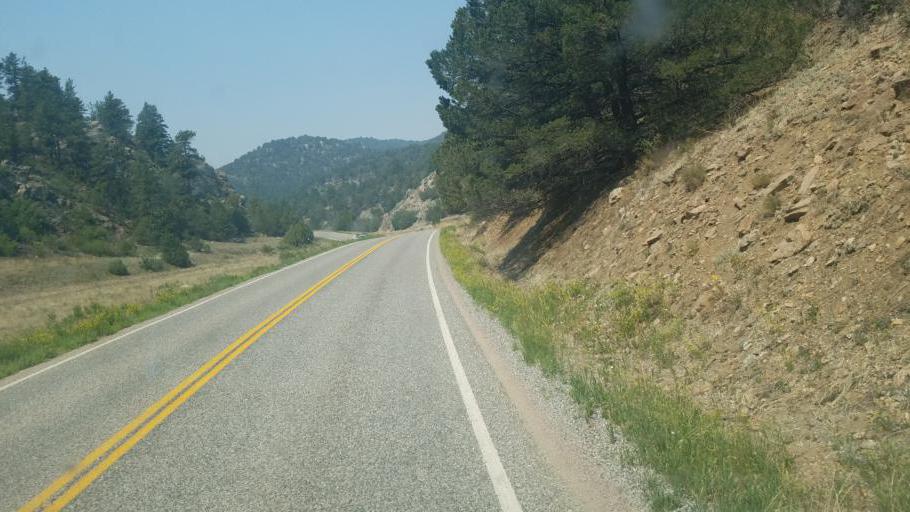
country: US
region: Colorado
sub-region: Fremont County
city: Canon City
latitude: 38.3896
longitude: -105.4527
